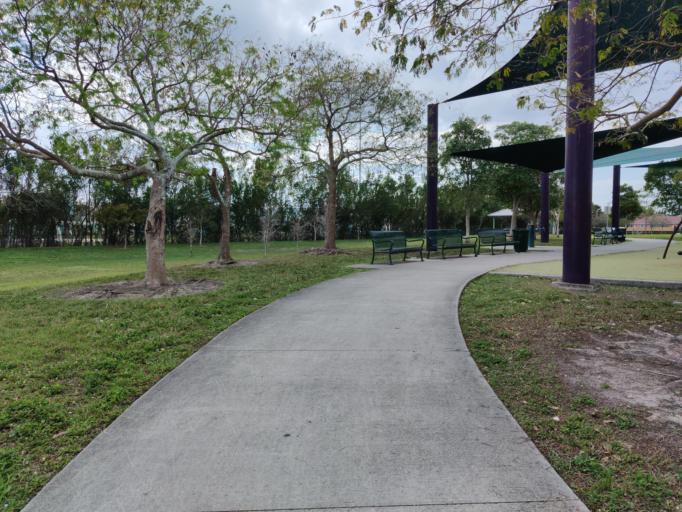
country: US
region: Florida
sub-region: Miami-Dade County
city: Kendall West
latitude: 25.7192
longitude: -80.4537
